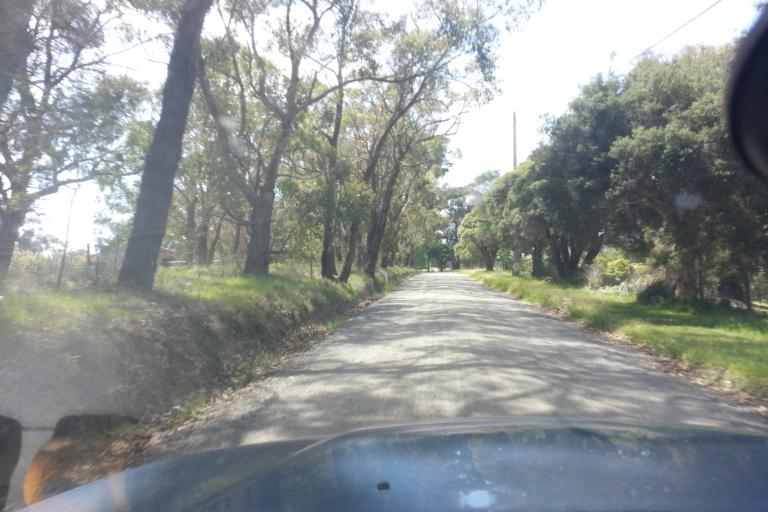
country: AU
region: Victoria
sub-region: Cardinia
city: Pakenham Upper
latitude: -37.9972
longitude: 145.4895
